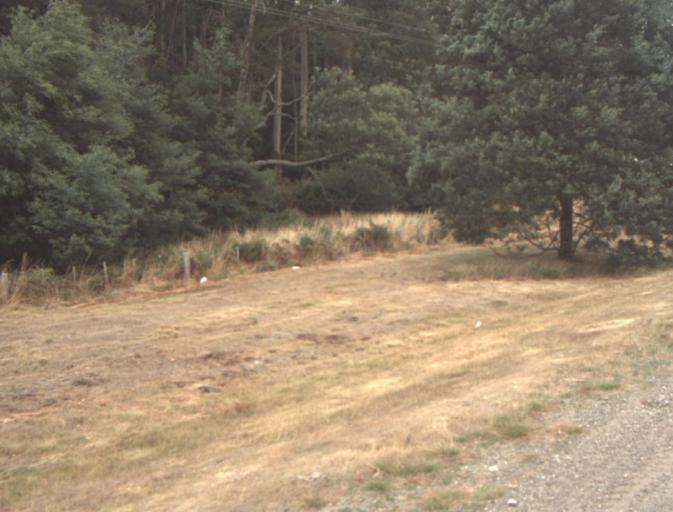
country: AU
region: Tasmania
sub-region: Launceston
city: Mayfield
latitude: -41.2812
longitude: 147.2195
